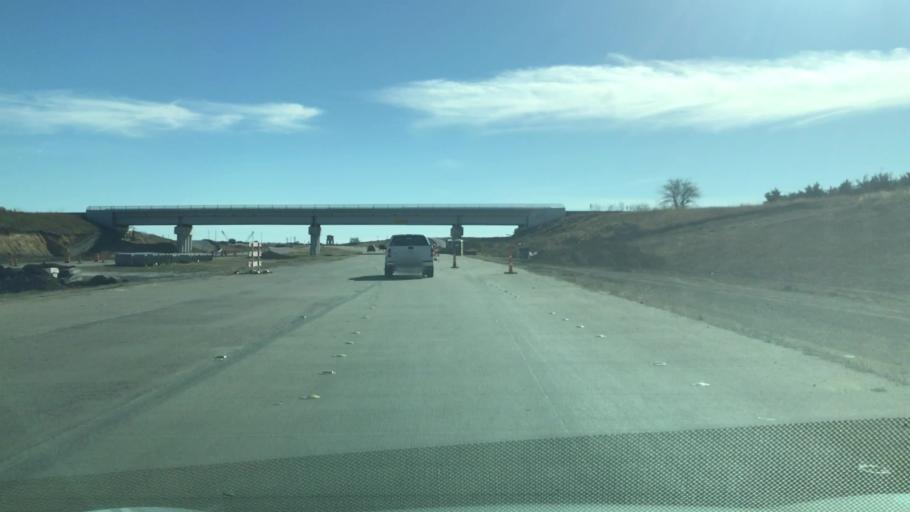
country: US
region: Texas
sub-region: Tarrant County
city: Mansfield
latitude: 32.5557
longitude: -97.0864
